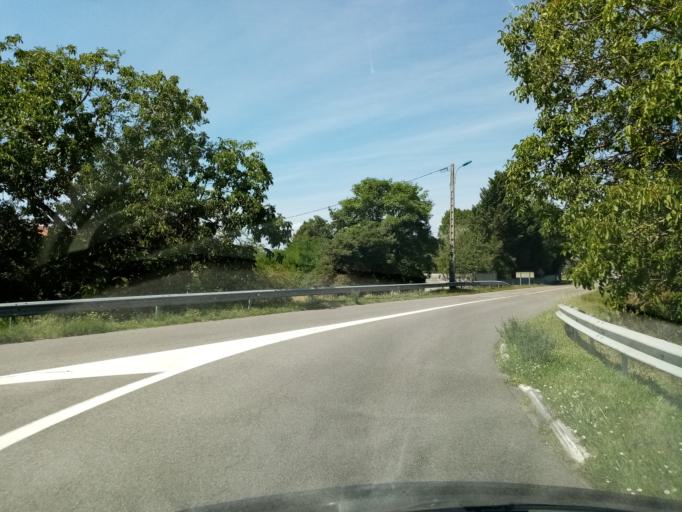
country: FR
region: Alsace
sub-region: Departement du Haut-Rhin
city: Neuf-Brisach
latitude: 48.0239
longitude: 7.5342
